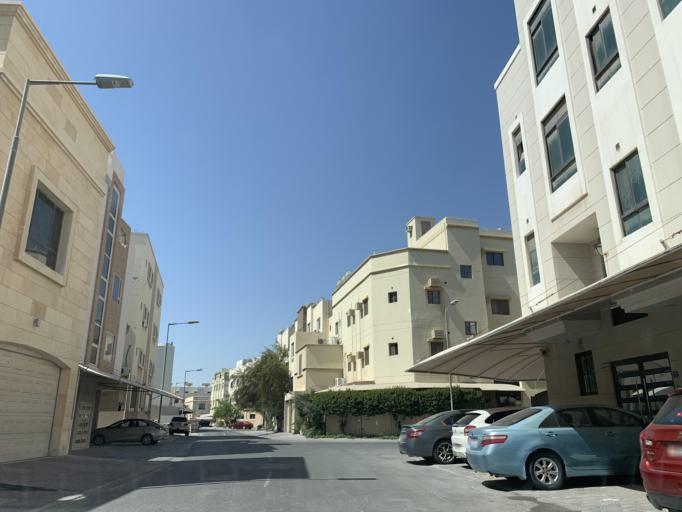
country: BH
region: Manama
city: Jidd Hafs
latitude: 26.2002
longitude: 50.5618
